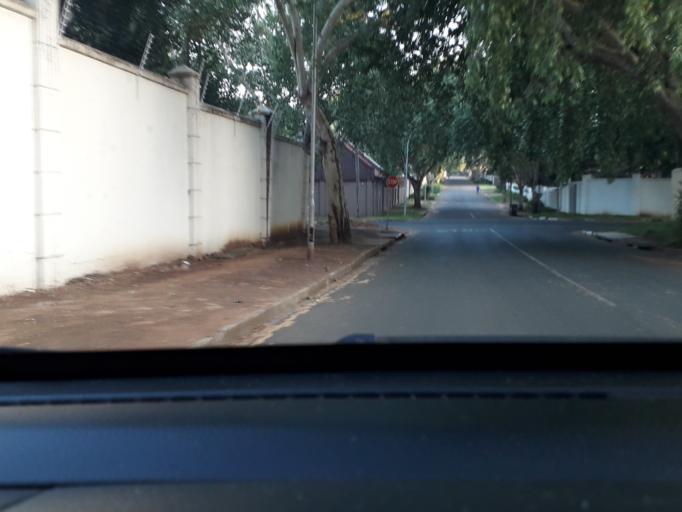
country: ZA
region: Gauteng
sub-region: City of Johannesburg Metropolitan Municipality
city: Johannesburg
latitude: -26.1561
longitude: 28.0515
